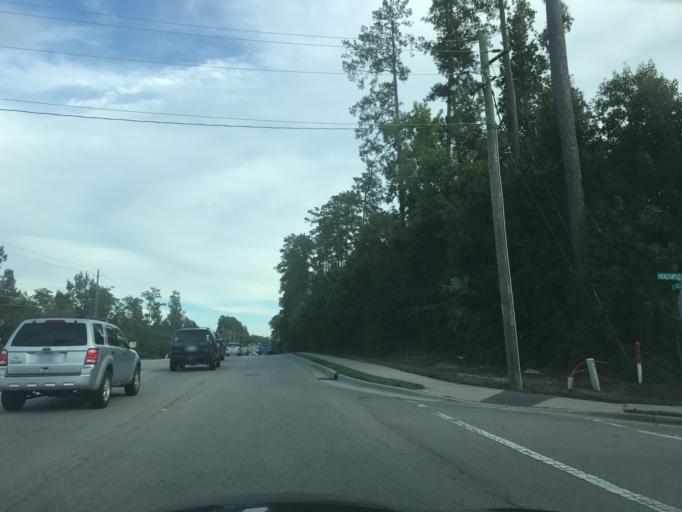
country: US
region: North Carolina
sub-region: Wake County
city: Apex
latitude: 35.7411
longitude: -78.8680
